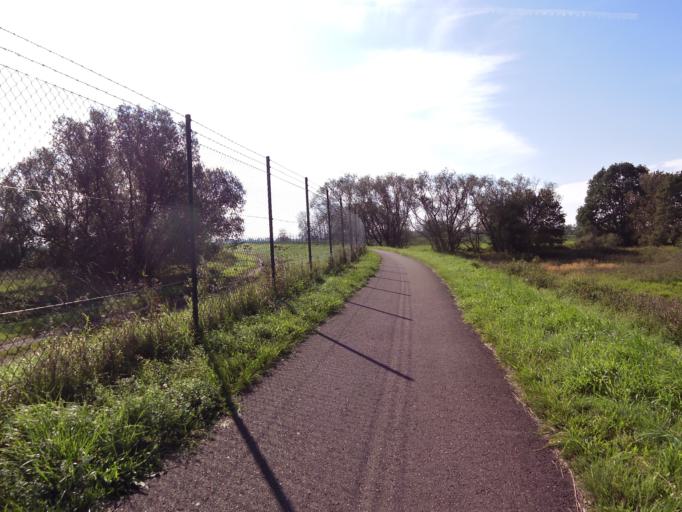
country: DE
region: Saxony-Anhalt
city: Coswig
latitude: 51.8717
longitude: 12.5184
